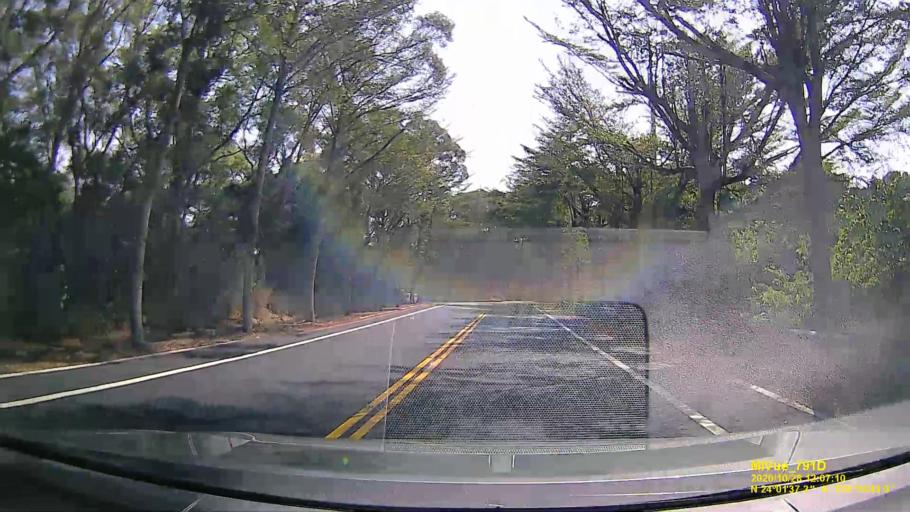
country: TW
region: Taiwan
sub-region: Changhua
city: Chang-hua
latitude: 24.0270
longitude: 120.5953
